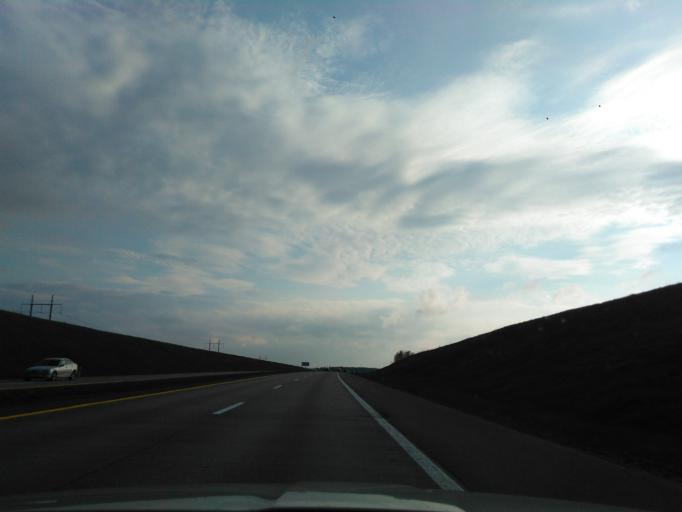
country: BY
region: Minsk
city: Astrashytski Haradok
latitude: 54.0995
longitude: 27.7900
